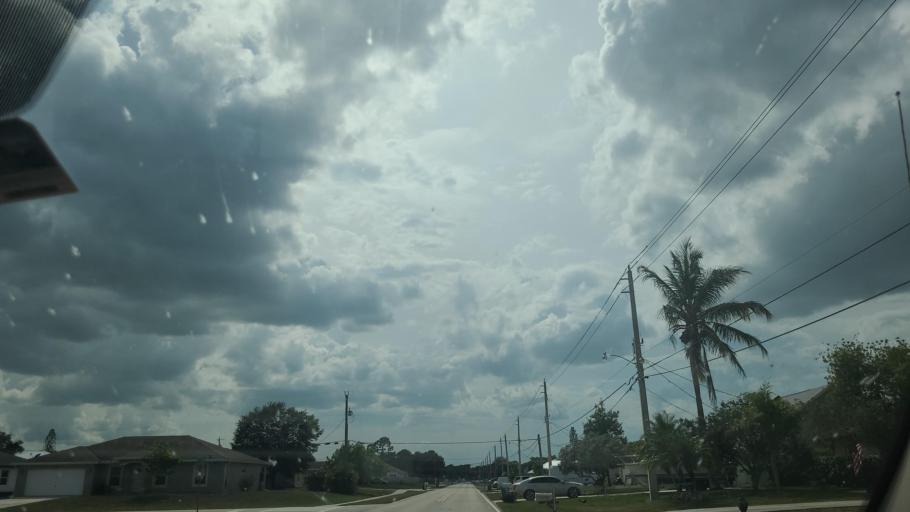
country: US
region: Florida
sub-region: Saint Lucie County
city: Port Saint Lucie
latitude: 27.2425
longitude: -80.3693
